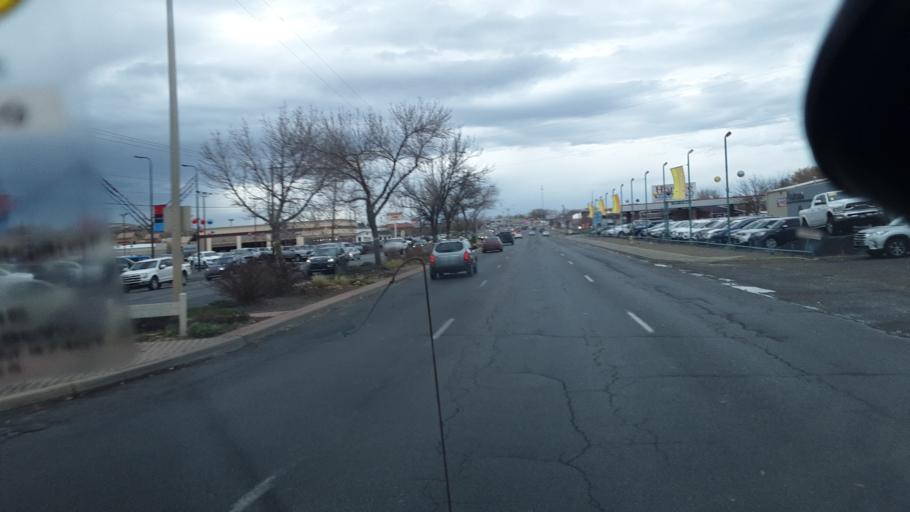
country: US
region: New Mexico
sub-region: San Juan County
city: Farmington
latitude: 36.7475
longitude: -108.1621
